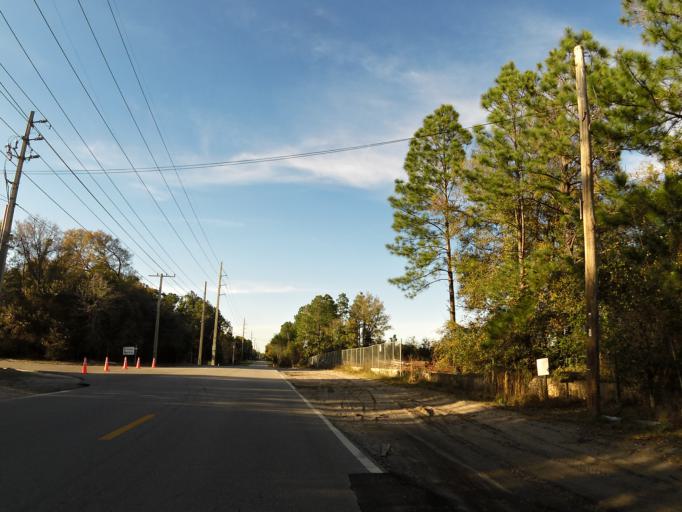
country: US
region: Florida
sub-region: Duval County
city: Jacksonville
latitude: 30.4277
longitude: -81.6023
